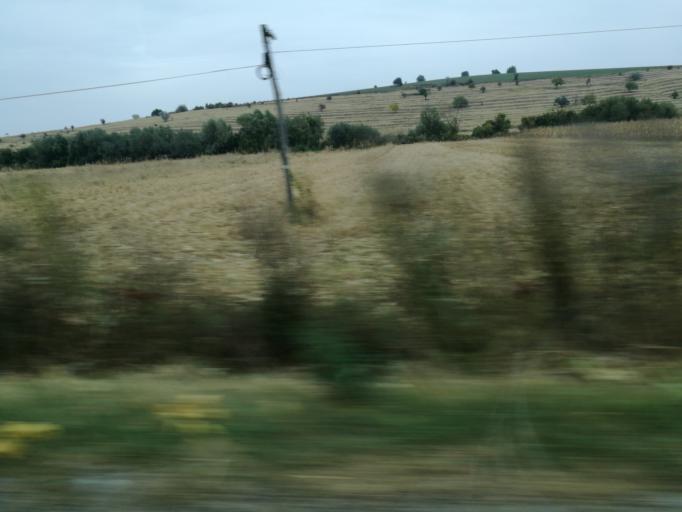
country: RO
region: Tulcea
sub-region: Comuna Ciucurova
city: Ciucurova
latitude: 44.9222
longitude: 28.4546
